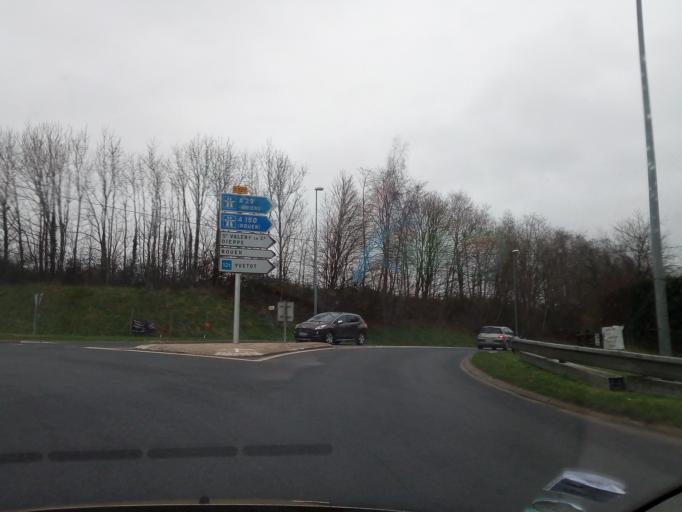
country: FR
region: Haute-Normandie
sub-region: Departement de la Seine-Maritime
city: Auzebosc
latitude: 49.6067
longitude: 0.7414
